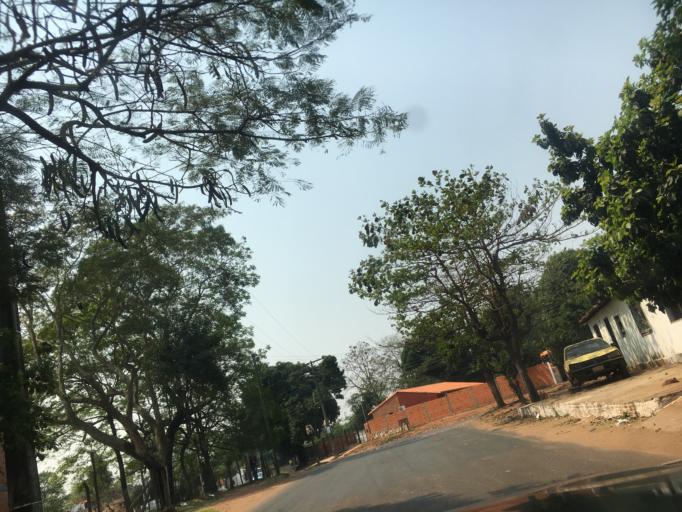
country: PY
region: Central
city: Villa Elisa
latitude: -25.3738
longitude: -57.5909
